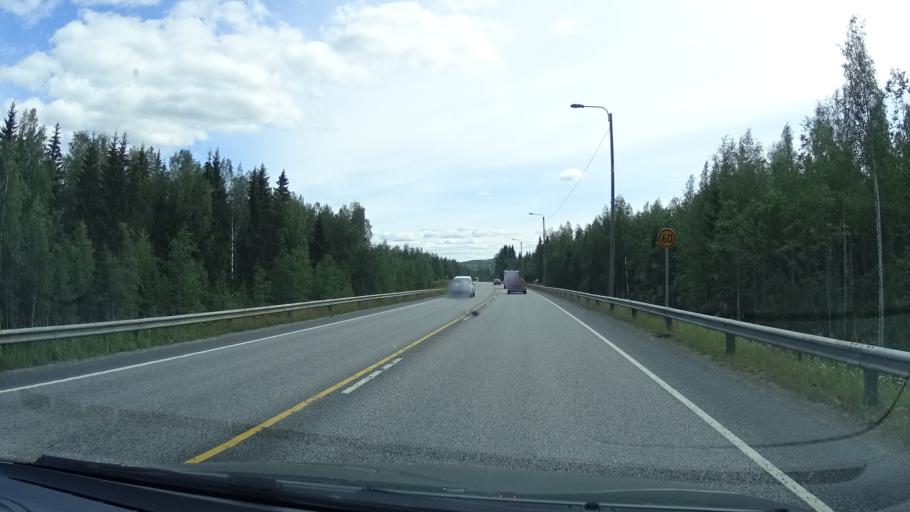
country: FI
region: Central Finland
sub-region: Jyvaeskylae
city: Jyvaeskylae
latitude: 62.2612
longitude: 25.5947
